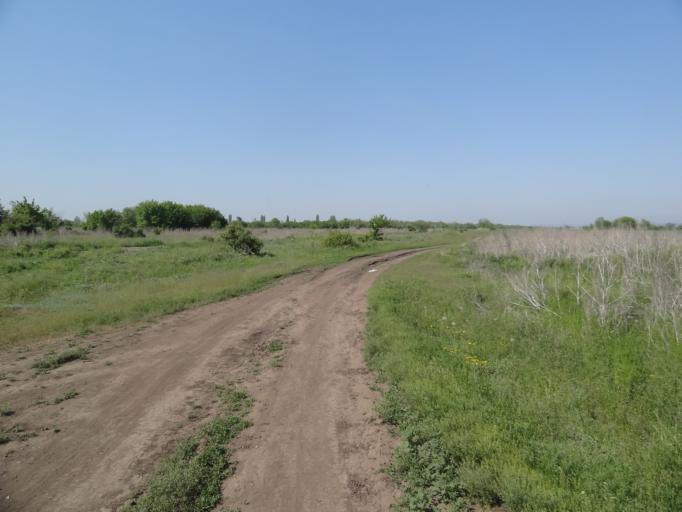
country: RU
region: Saratov
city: Privolzhskiy
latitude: 51.4175
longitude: 46.1072
